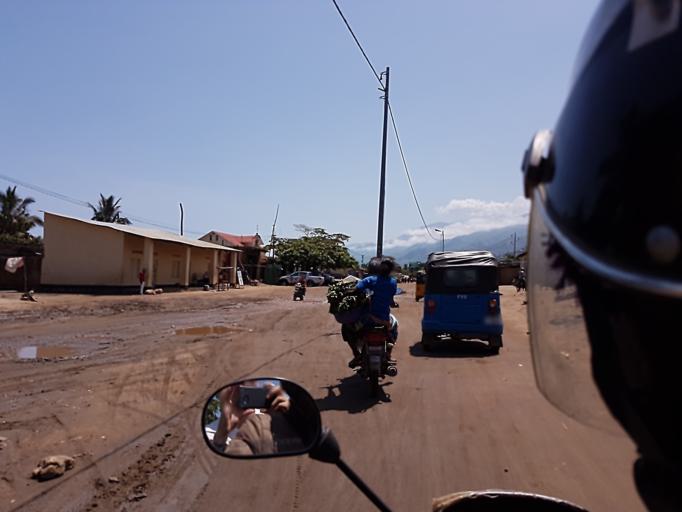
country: CD
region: South Kivu
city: Uvira
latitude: -3.3663
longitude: 29.1484
